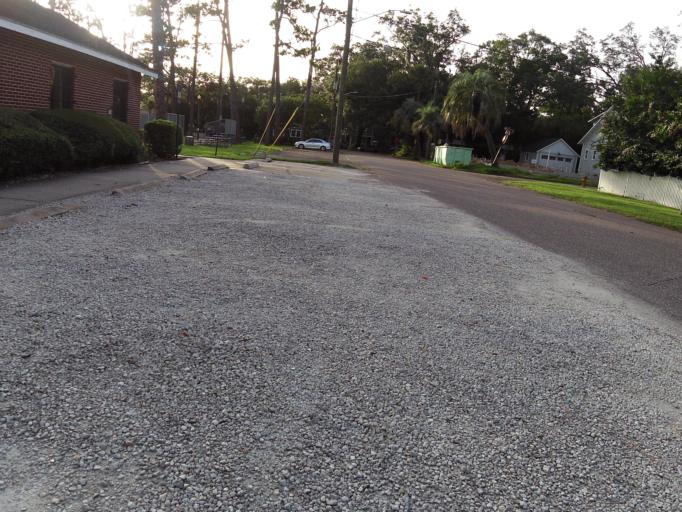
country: US
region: Florida
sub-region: Duval County
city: Jacksonville
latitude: 30.2987
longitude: -81.7114
